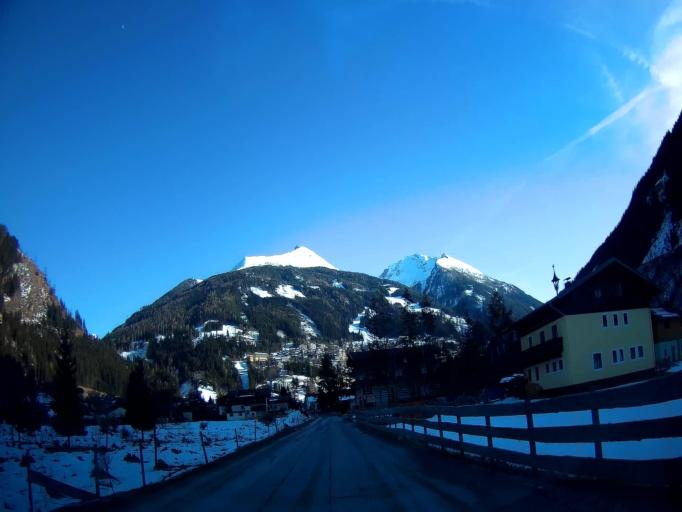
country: AT
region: Salzburg
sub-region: Politischer Bezirk Sankt Johann im Pongau
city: Bad Gastein
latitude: 47.1324
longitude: 13.1325
